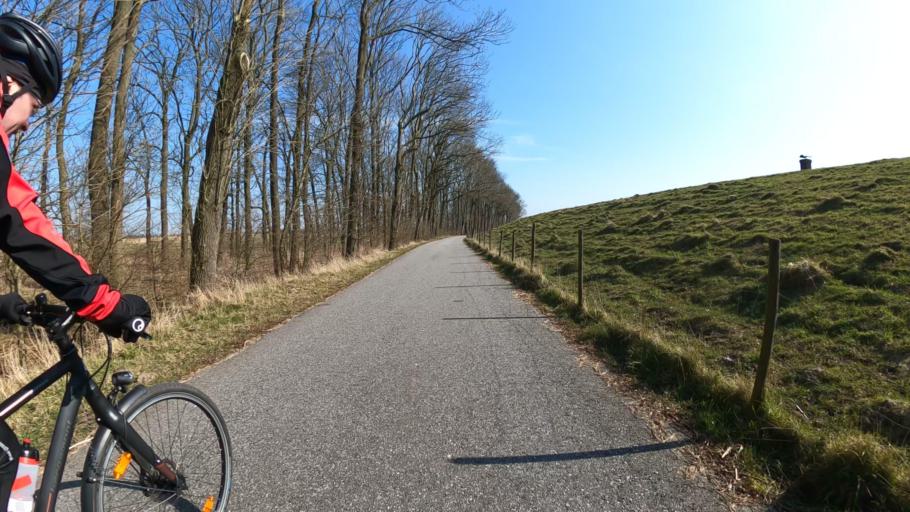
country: DE
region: Schleswig-Holstein
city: Seestermuhe
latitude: 53.6645
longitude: 9.5608
